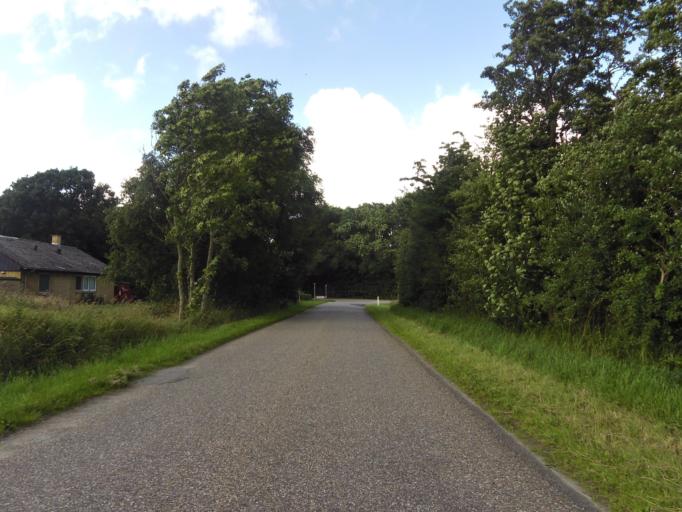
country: DK
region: South Denmark
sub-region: Tonder Kommune
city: Toftlund
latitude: 55.1482
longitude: 9.0856
